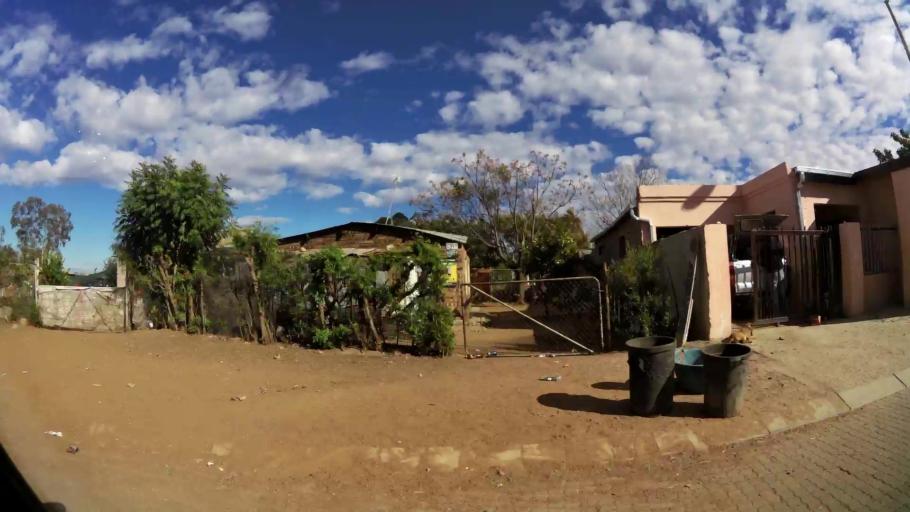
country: ZA
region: Limpopo
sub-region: Waterberg District Municipality
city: Warmbaths
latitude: -24.8802
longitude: 28.2717
